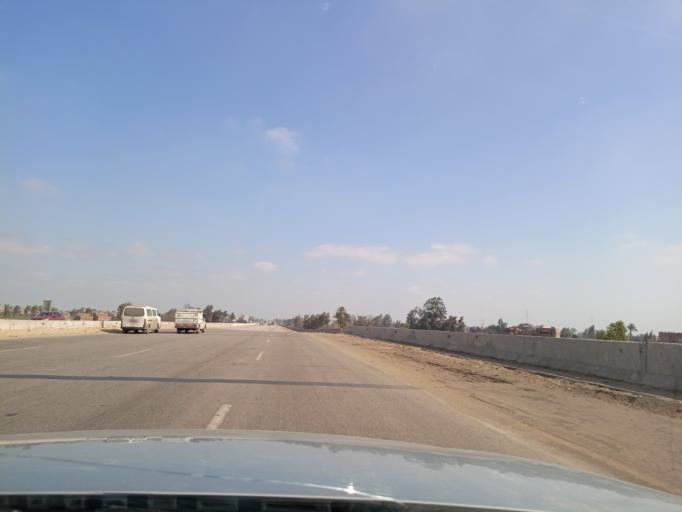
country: EG
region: Muhafazat al Minufiyah
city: Al Bajur
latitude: 30.4247
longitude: 31.0903
